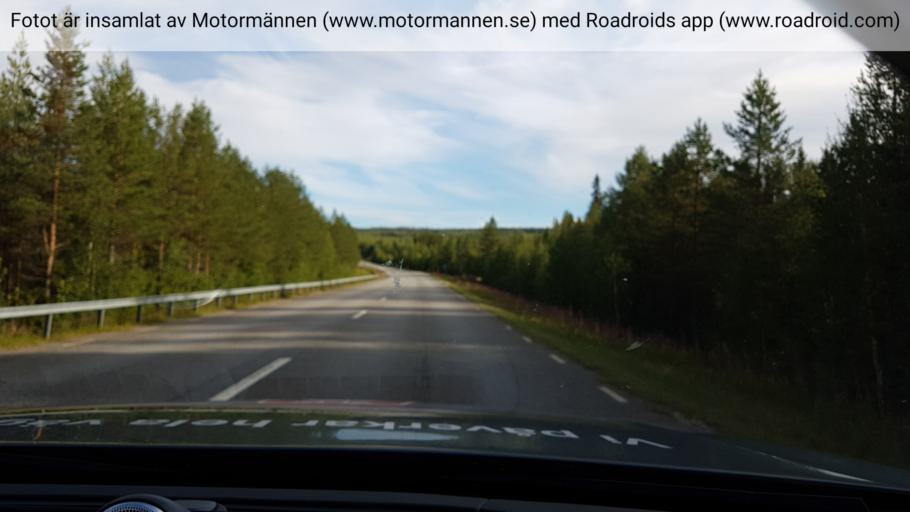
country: SE
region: Jaemtland
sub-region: Stroemsunds Kommun
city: Stroemsund
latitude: 64.2420
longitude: 15.4518
